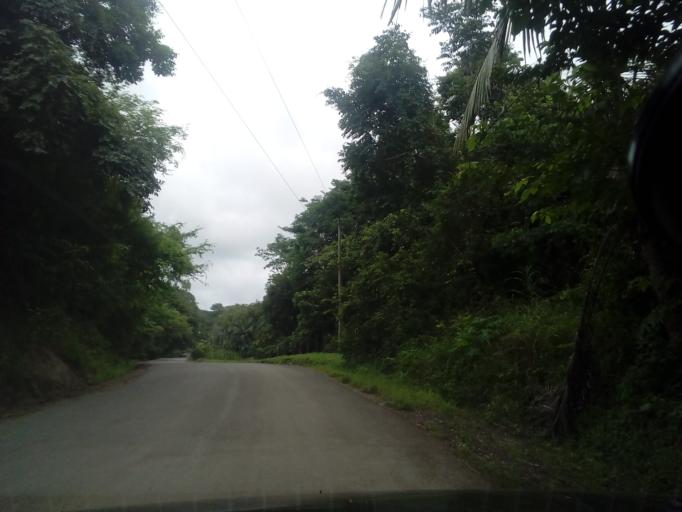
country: CR
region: Guanacaste
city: Samara
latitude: 9.9169
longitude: -85.5501
